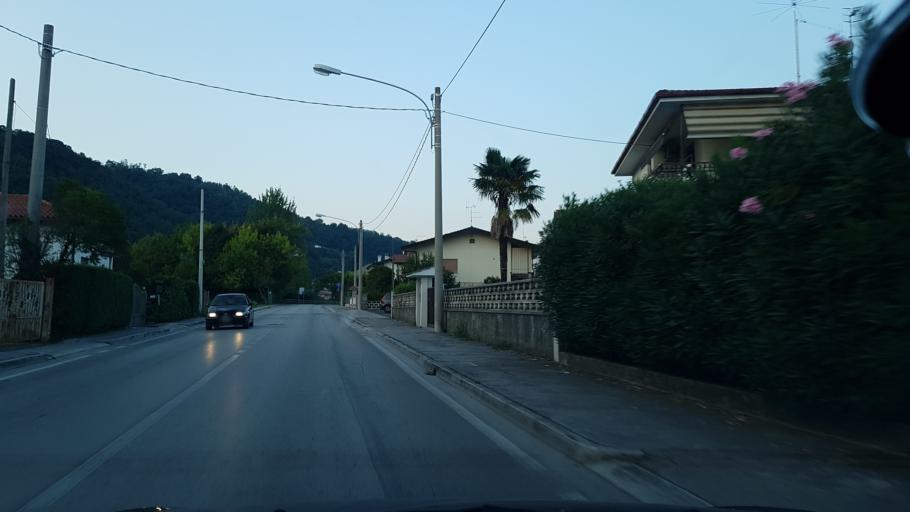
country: IT
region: Friuli Venezia Giulia
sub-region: Provincia di Gorizia
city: Gorizia
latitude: 45.9428
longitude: 13.5991
